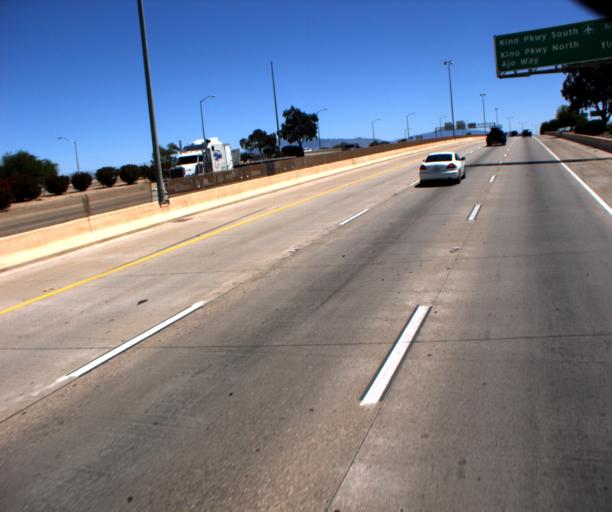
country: US
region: Arizona
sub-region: Pima County
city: South Tucson
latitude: 32.1857
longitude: -110.9630
